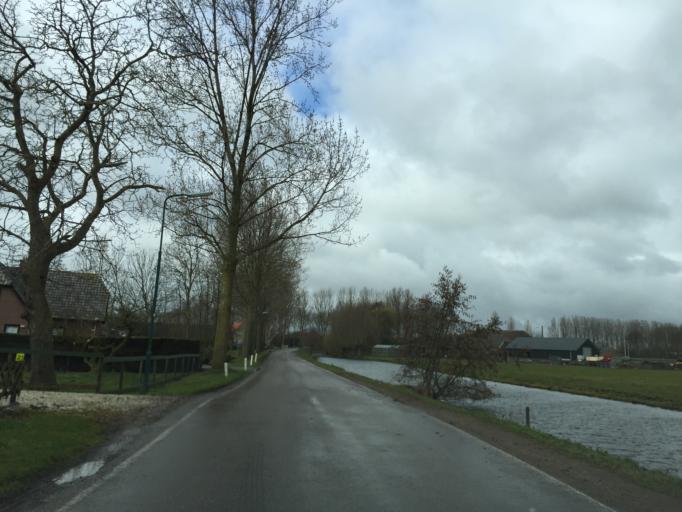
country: NL
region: Utrecht
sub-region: Gemeente Montfoort
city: Montfoort
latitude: 52.0785
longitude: 4.9701
